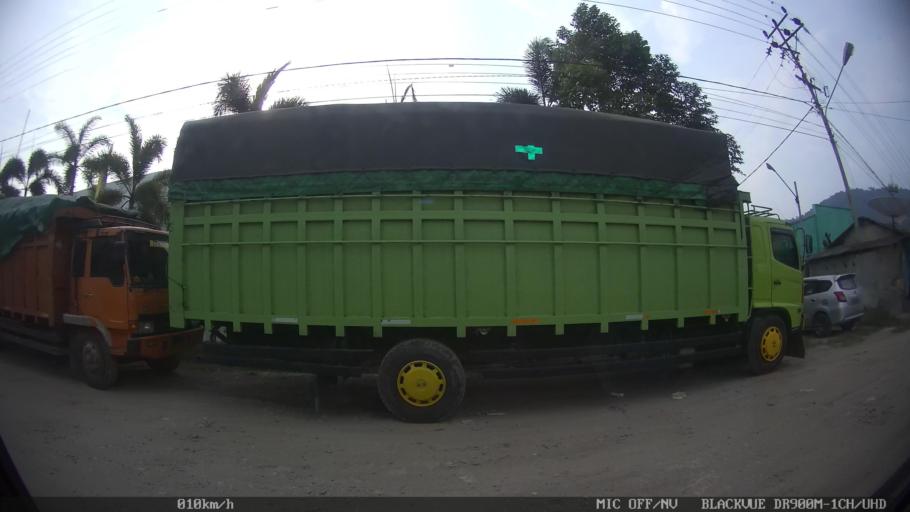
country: ID
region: Lampung
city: Panjang
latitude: -5.4487
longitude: 105.3096
